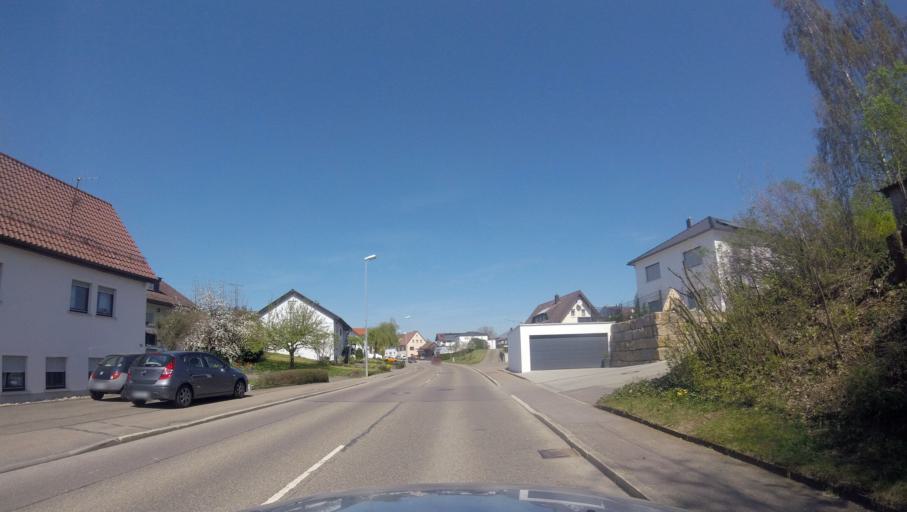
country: DE
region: Baden-Wuerttemberg
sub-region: Regierungsbezirk Stuttgart
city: Mutlangen
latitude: 48.8273
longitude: 9.7949
